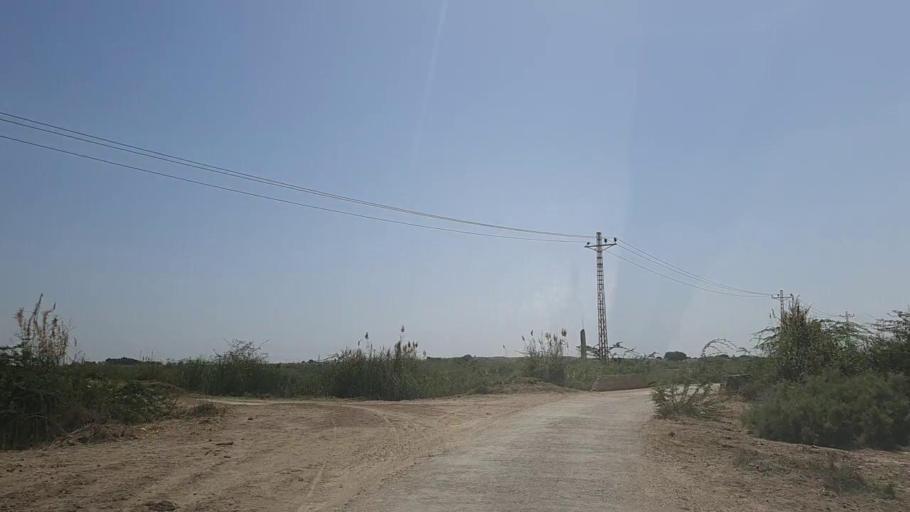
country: PK
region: Sindh
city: Gharo
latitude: 24.7680
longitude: 67.7517
